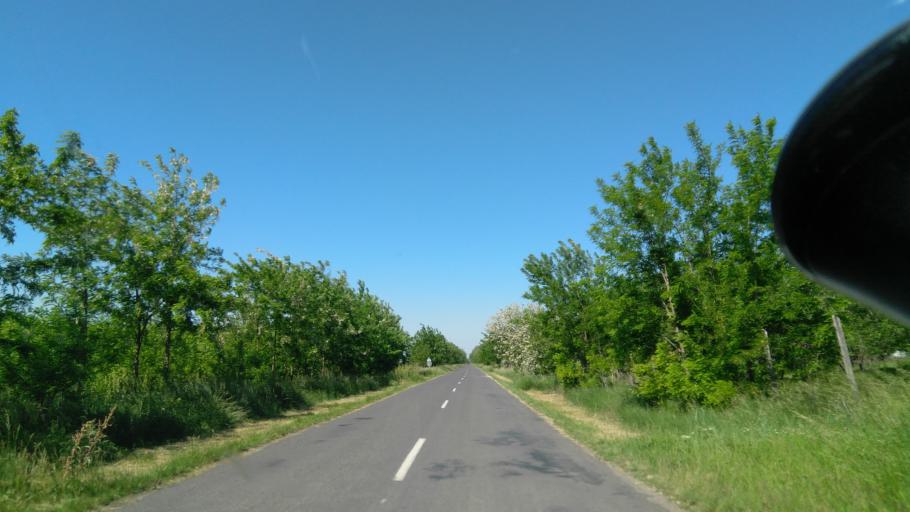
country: HU
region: Bekes
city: Kevermes
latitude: 46.4262
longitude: 21.1600
